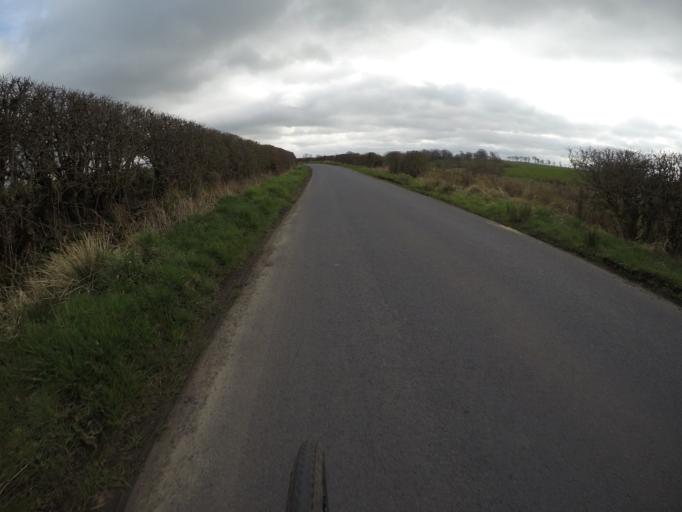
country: GB
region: Scotland
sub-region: North Ayrshire
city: Springside
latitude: 55.6651
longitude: -4.5979
